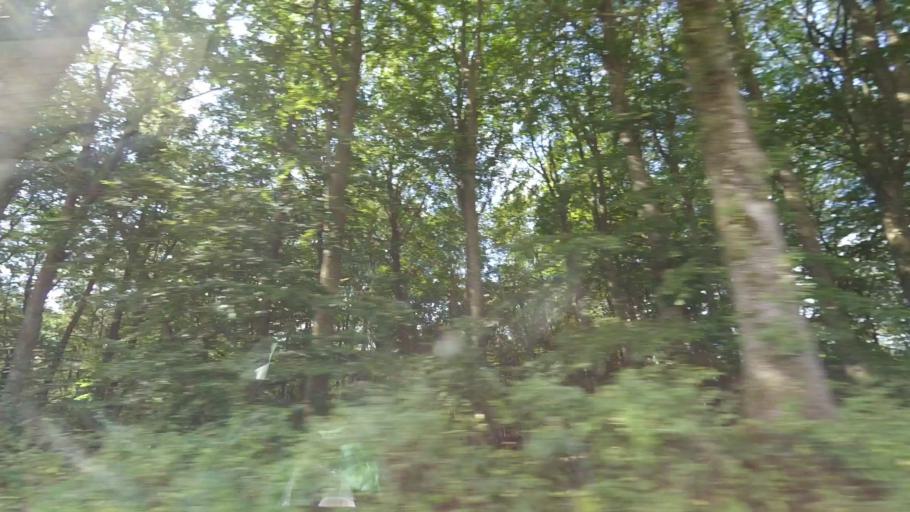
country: DK
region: Central Jutland
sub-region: Syddjurs Kommune
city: Ryomgard
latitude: 56.4647
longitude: 10.5223
